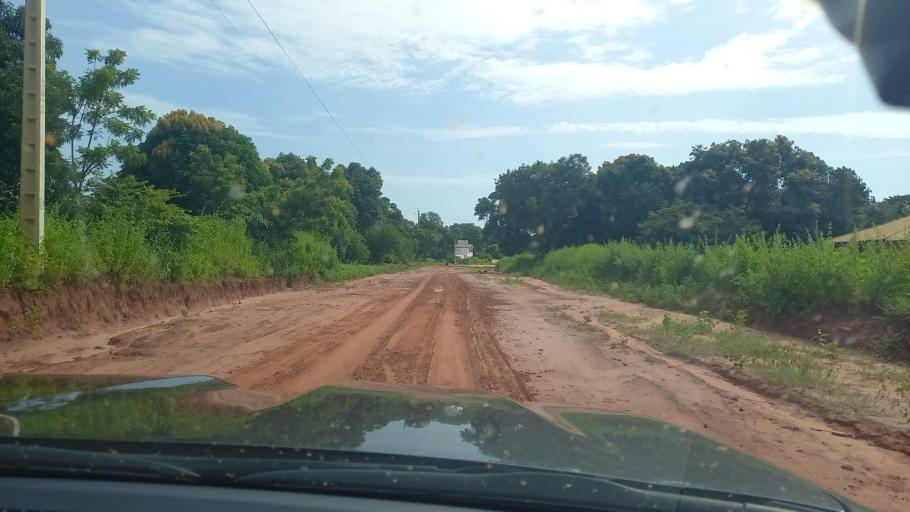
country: SN
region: Ziguinchor
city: Ziguinchor
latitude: 12.6727
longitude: -16.2115
